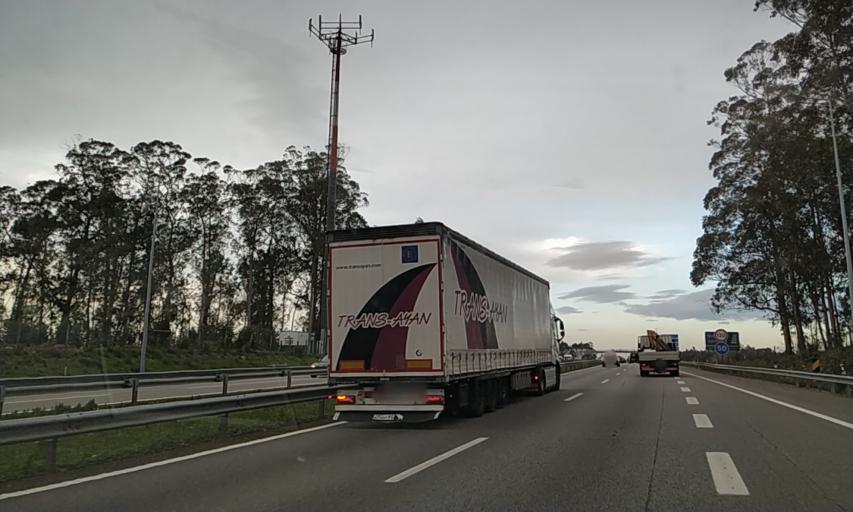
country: PT
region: Porto
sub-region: Matosinhos
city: Lavra
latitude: 41.2632
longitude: -8.7014
